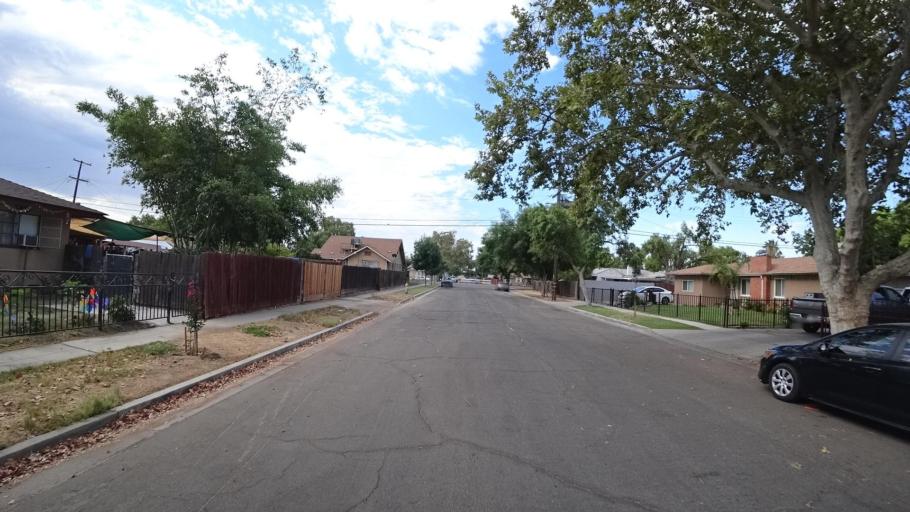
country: US
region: California
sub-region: Fresno County
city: Fresno
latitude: 36.7621
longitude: -119.7658
